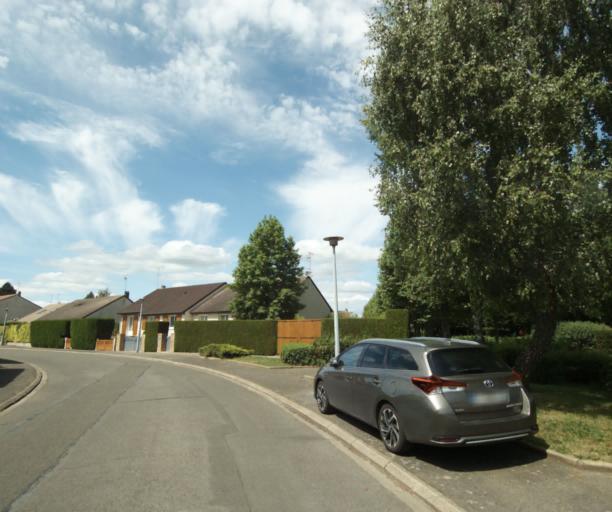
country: FR
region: Centre
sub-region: Departement d'Eure-et-Loir
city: Luce
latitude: 48.4336
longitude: 1.4517
